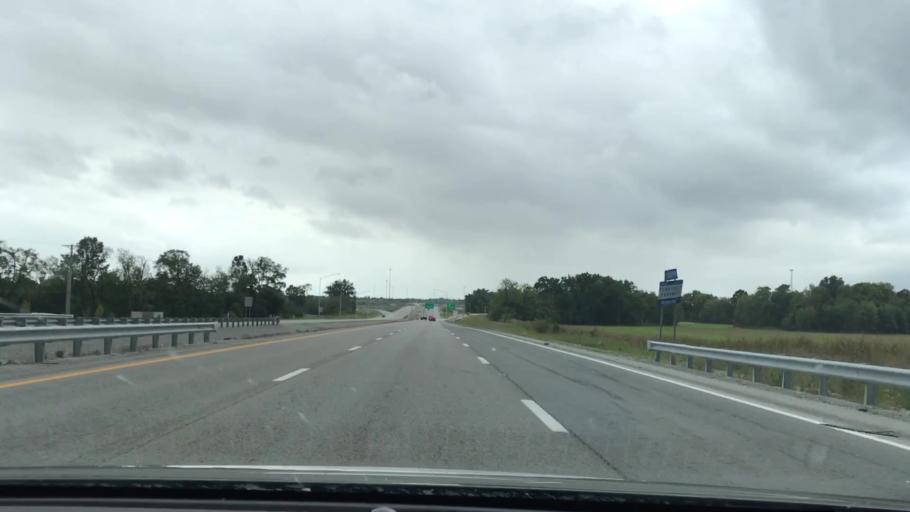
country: US
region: Kentucky
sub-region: Christian County
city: Hopkinsville
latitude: 36.8263
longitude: -87.4773
